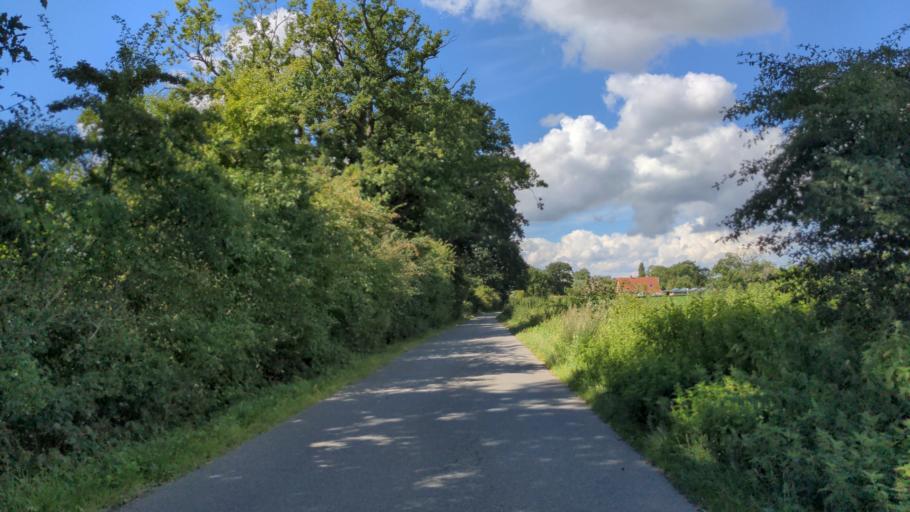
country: DE
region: Schleswig-Holstein
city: Beschendorf
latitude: 54.1751
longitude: 10.8498
